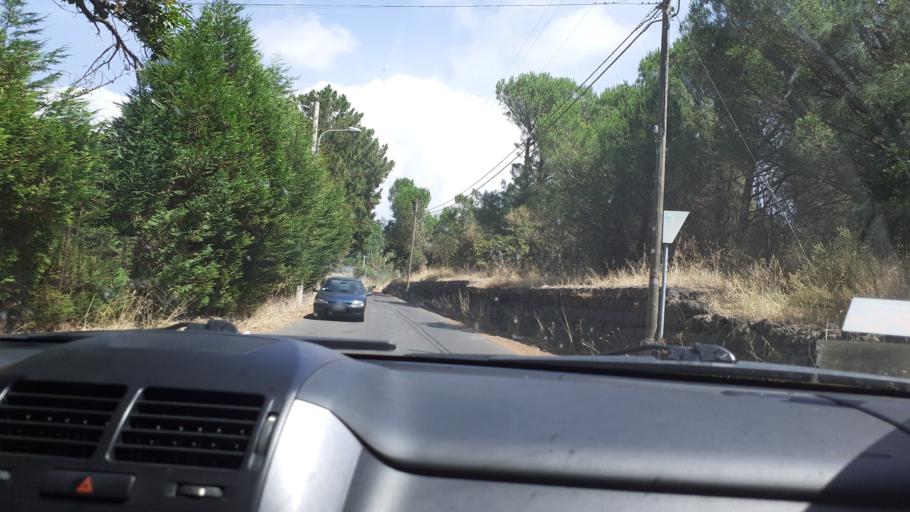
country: IT
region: Sicily
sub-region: Catania
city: Nicolosi
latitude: 37.6304
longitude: 15.0245
